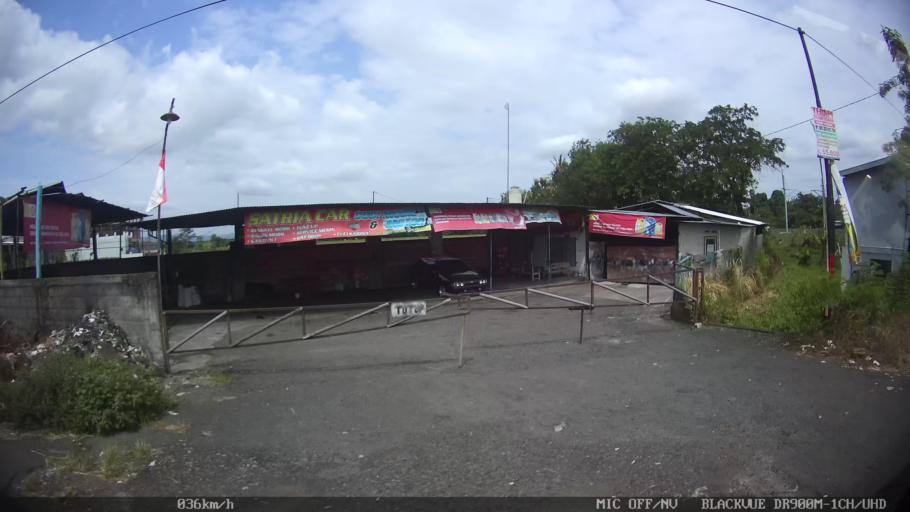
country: ID
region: Central Java
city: Candi Prambanan
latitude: -7.7726
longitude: 110.4698
